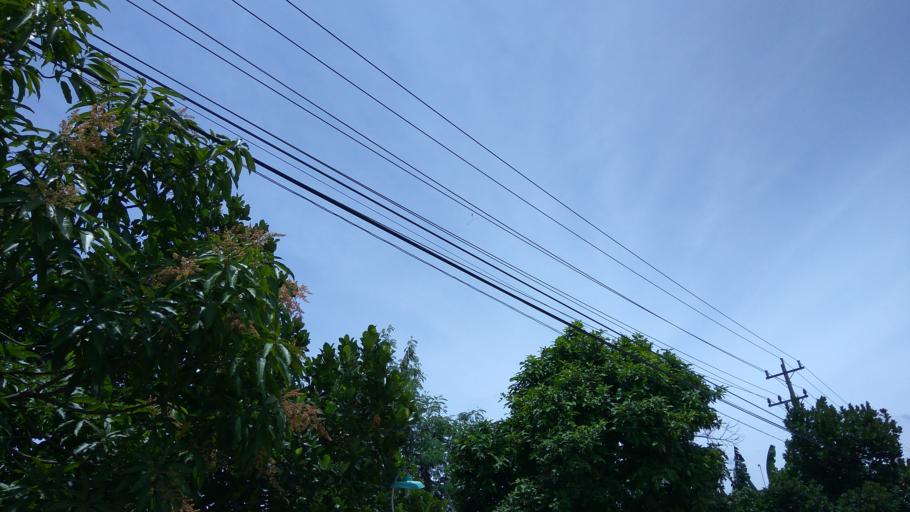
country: ID
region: Central Java
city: Mranggen
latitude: -7.0423
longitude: 110.5685
